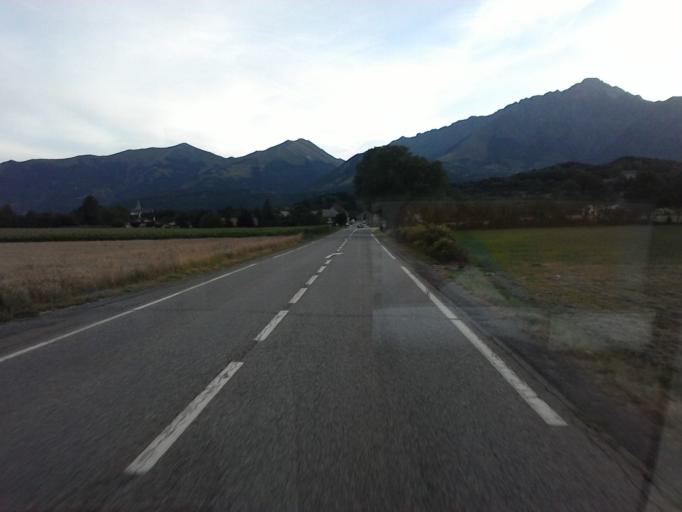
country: FR
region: Provence-Alpes-Cote d'Azur
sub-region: Departement des Hautes-Alpes
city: Saint-Bonnet-en-Champsaur
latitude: 44.7491
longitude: 6.0083
